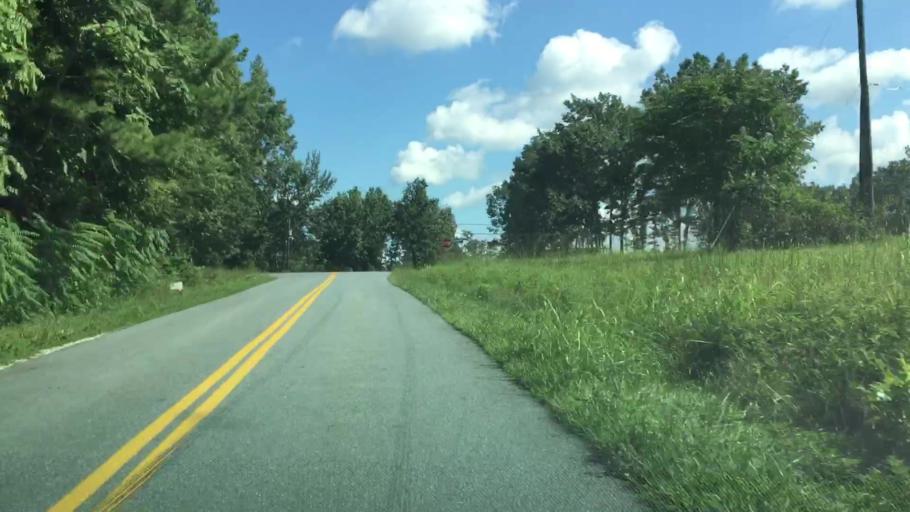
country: US
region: Virginia
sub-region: Appomattox County
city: Appomattox
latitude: 37.3153
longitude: -78.8441
